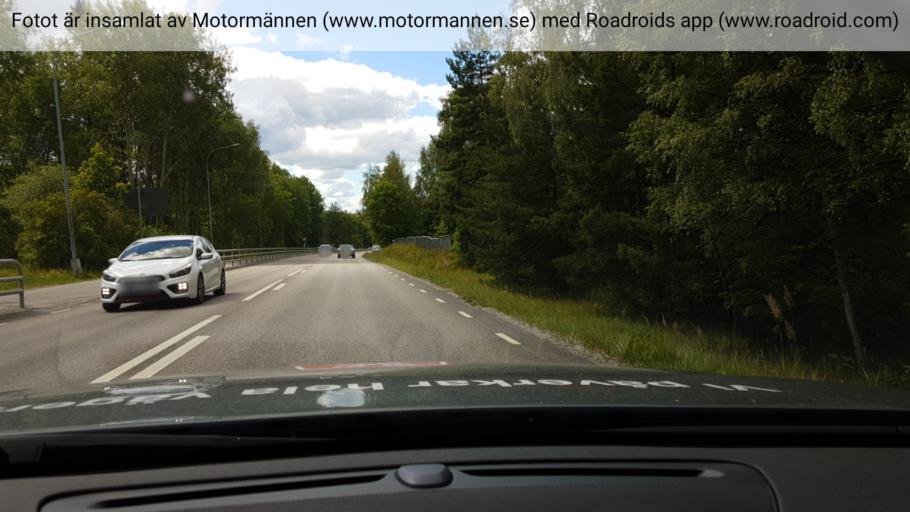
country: SE
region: Stockholm
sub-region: Vallentuna Kommun
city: Vallentuna
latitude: 59.5305
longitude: 18.0951
